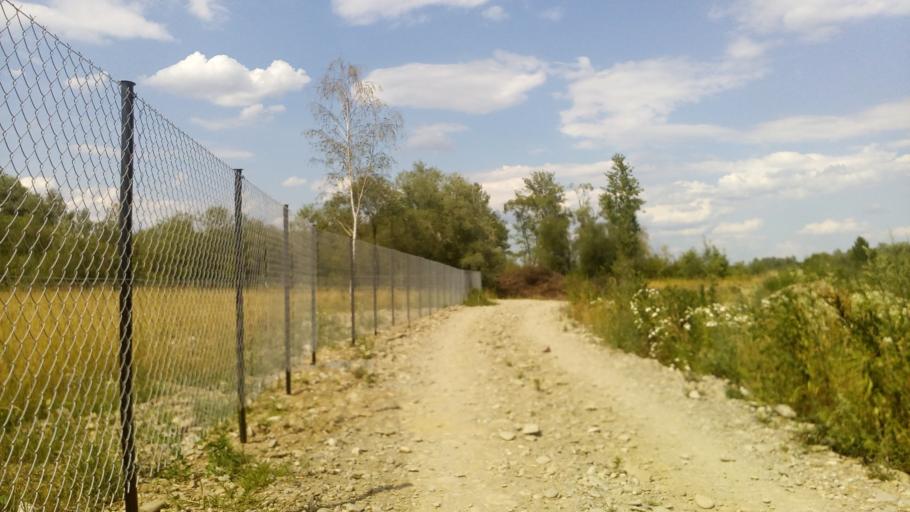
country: PL
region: Lesser Poland Voivodeship
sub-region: Powiat nowosadecki
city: Stary Sacz
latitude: 49.5811
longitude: 20.6457
